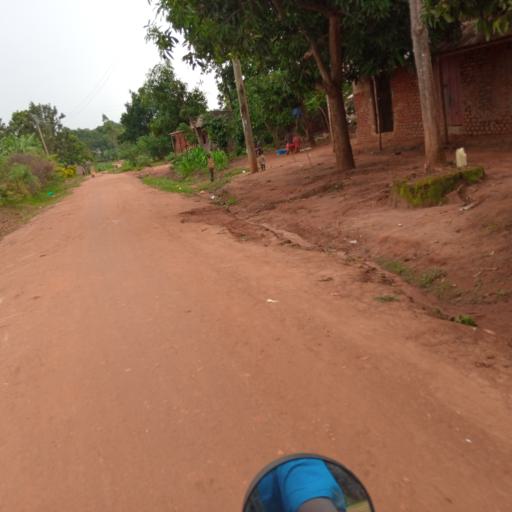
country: UG
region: Eastern Region
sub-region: Mbale District
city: Mbale
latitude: 1.1252
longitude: 34.1765
